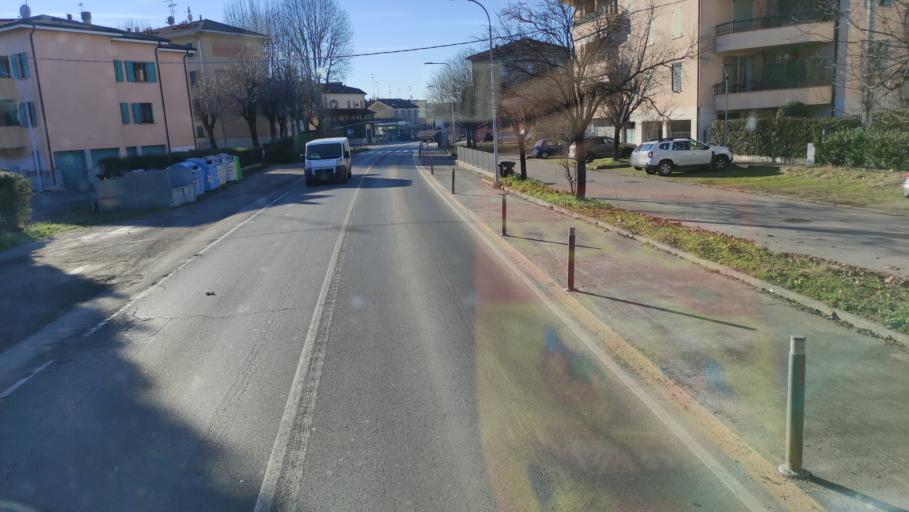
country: IT
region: Emilia-Romagna
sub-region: Provincia di Reggio Emilia
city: Novellara
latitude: 44.8484
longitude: 10.7296
